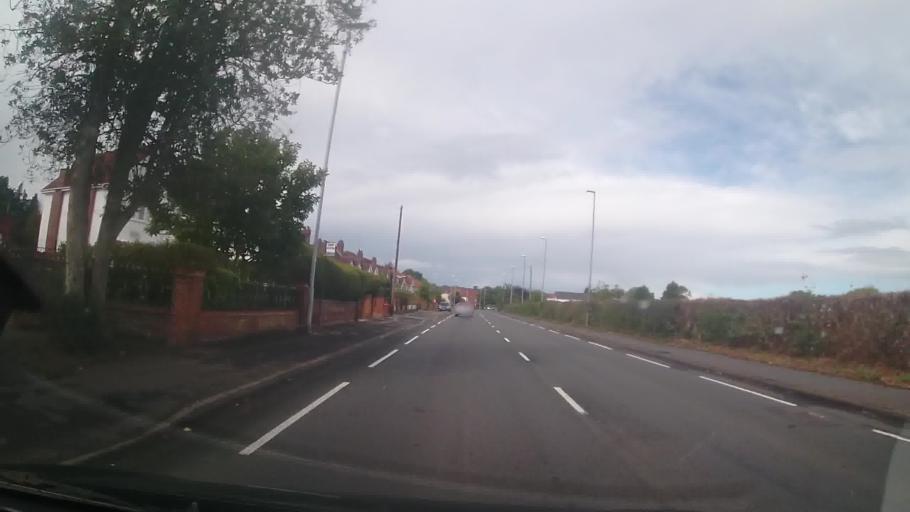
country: GB
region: England
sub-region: Worcestershire
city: Kidderminster
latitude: 52.3946
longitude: -2.2641
